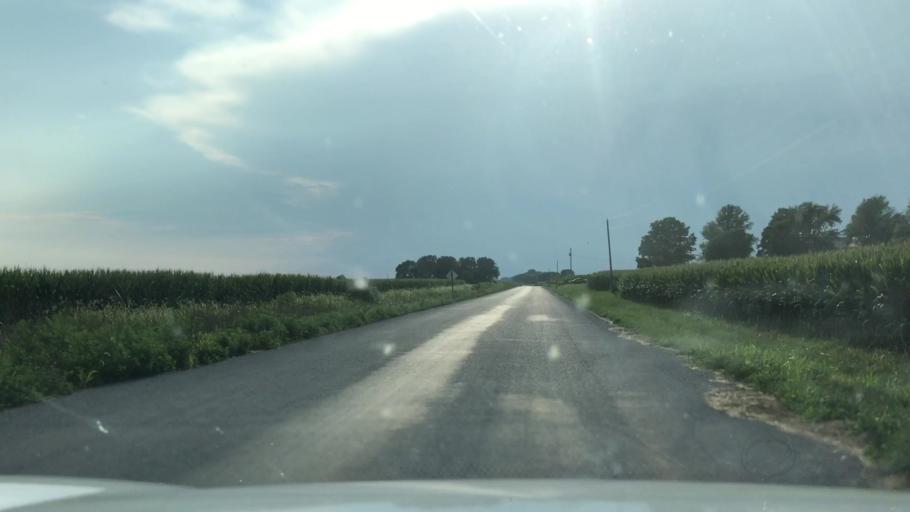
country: US
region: Illinois
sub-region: Washington County
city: Okawville
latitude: 38.4129
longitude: -89.4809
